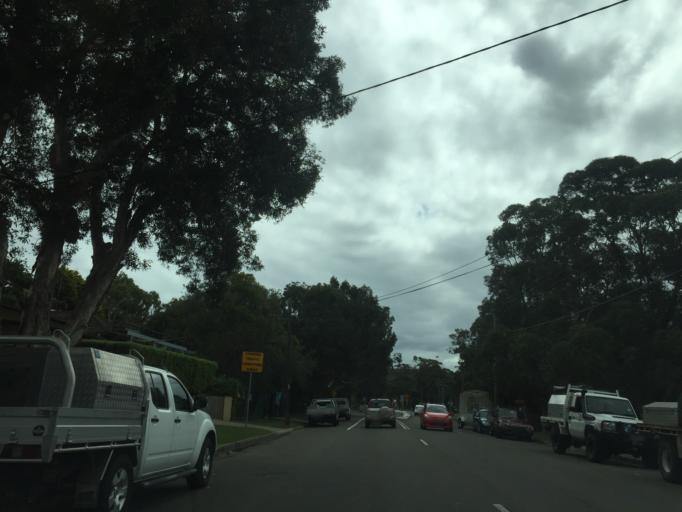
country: AU
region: New South Wales
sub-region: Pittwater
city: Warriewood
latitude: -33.6988
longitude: 151.2937
